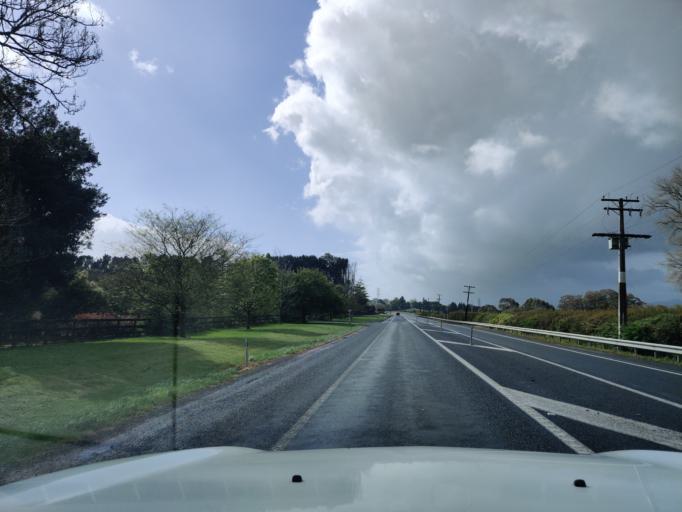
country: NZ
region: Waikato
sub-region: Waipa District
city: Cambridge
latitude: -37.9039
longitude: 175.5201
